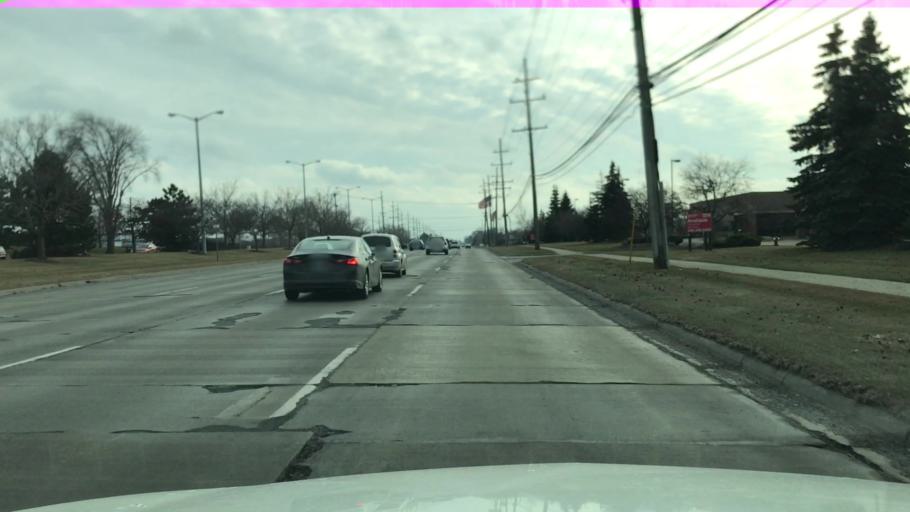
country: US
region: Michigan
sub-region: Macomb County
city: Sterling Heights
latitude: 42.5603
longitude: -83.0492
